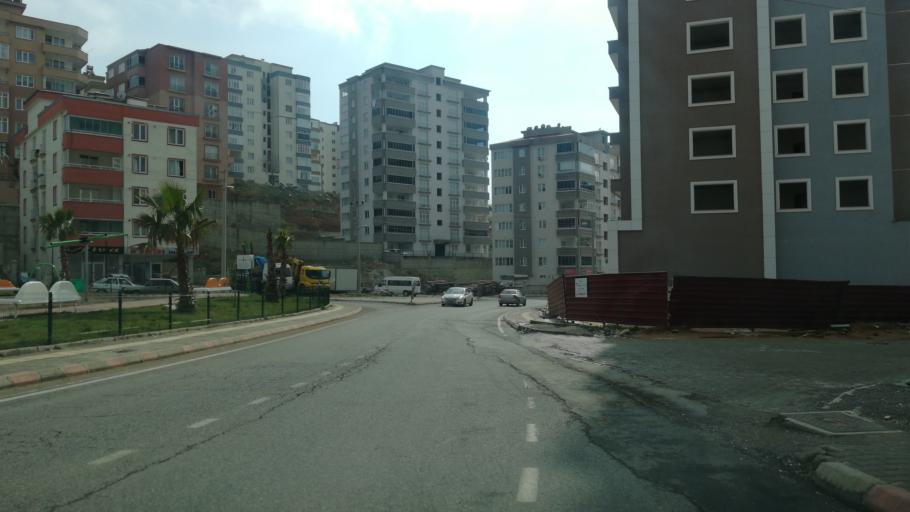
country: TR
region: Kahramanmaras
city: Kahramanmaras
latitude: 37.5818
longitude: 36.8981
